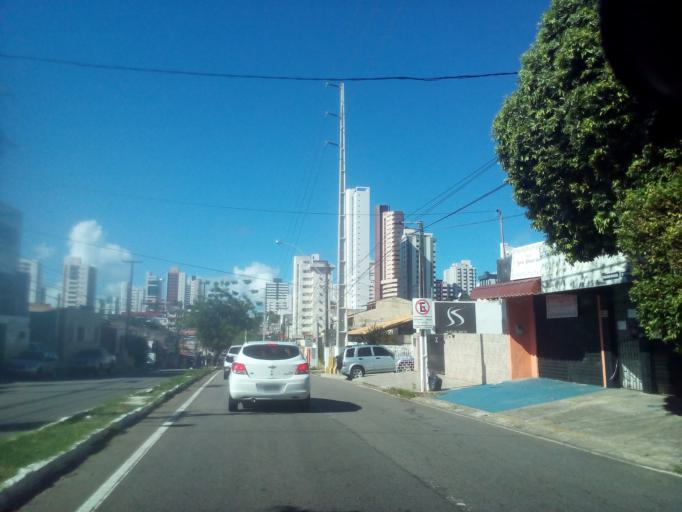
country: BR
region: Rio Grande do Norte
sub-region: Natal
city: Natal
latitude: -5.8075
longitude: -35.2065
